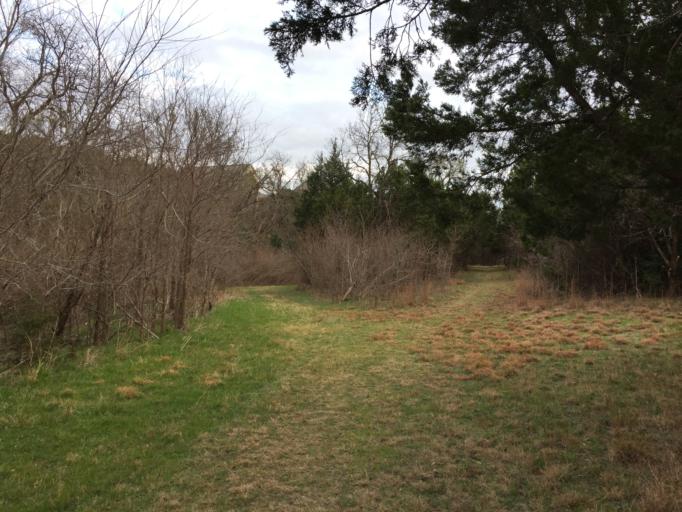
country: US
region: Texas
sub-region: Travis County
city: Wells Branch
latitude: 30.3936
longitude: -97.6785
